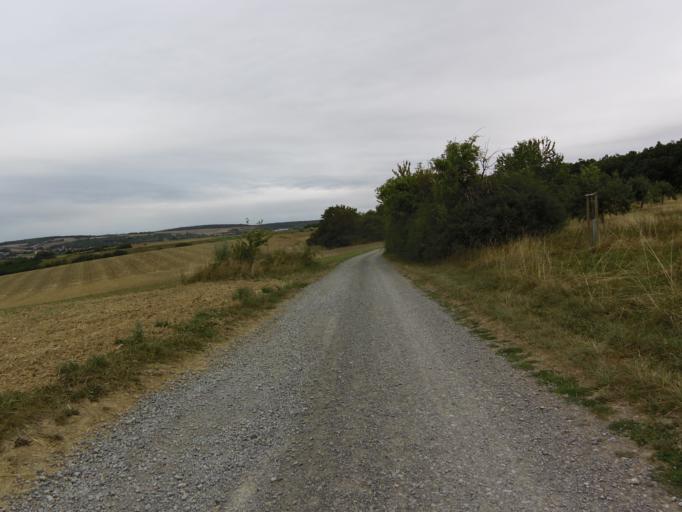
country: DE
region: Bavaria
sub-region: Regierungsbezirk Unterfranken
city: Rimpar
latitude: 49.8353
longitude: 9.9683
